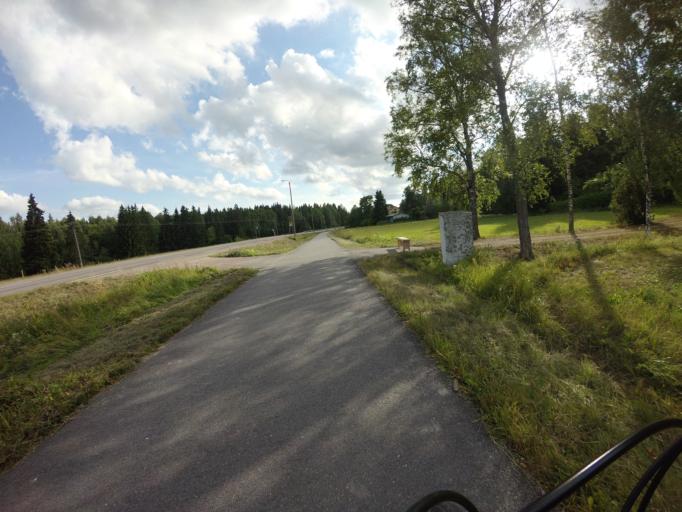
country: FI
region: Varsinais-Suomi
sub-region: Turku
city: Vahto
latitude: 60.5883
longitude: 22.3722
